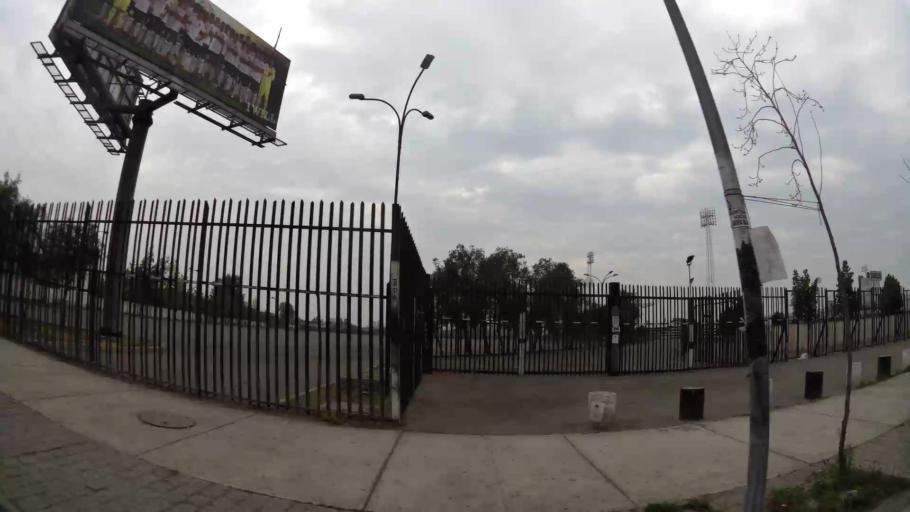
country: CL
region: Santiago Metropolitan
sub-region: Provincia de Santiago
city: Villa Presidente Frei, Nunoa, Santiago, Chile
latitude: -33.5085
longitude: -70.6081
